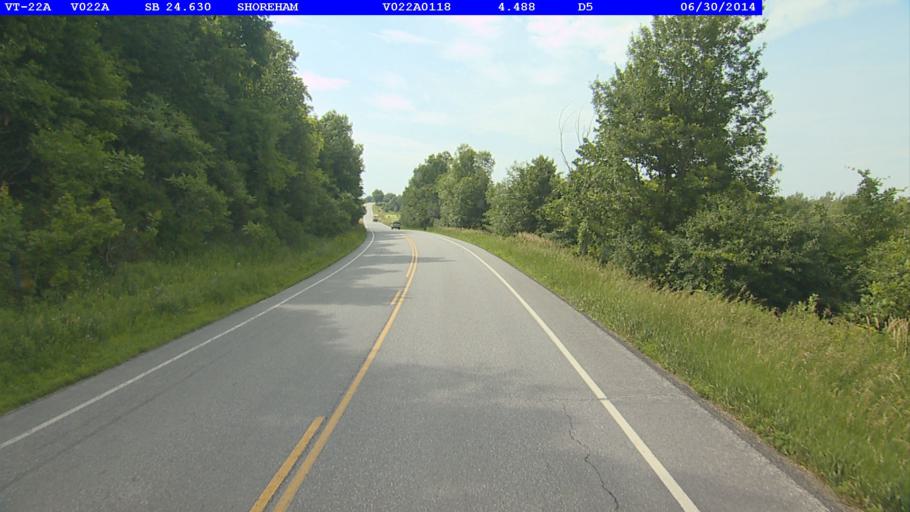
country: US
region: New York
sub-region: Essex County
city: Ticonderoga
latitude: 43.9138
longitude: -73.3120
